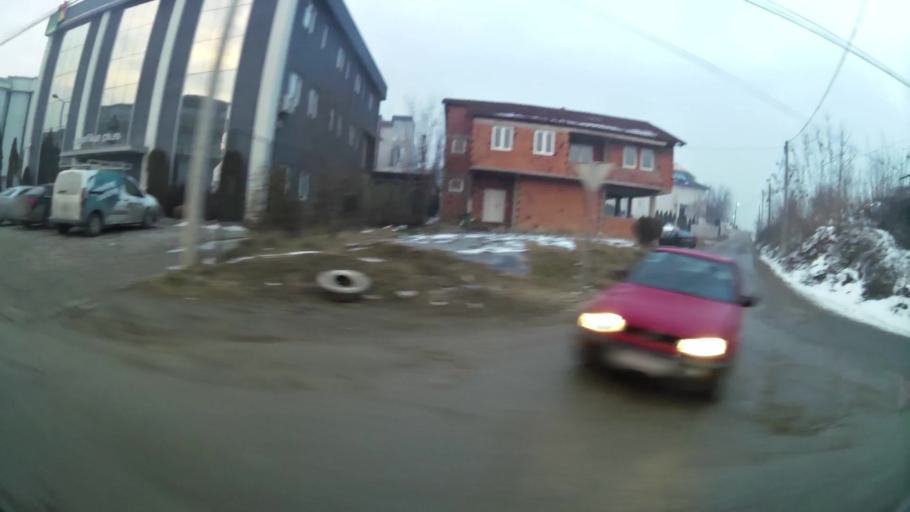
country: MK
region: Suto Orizari
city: Suto Orizare
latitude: 42.0273
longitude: 21.4100
